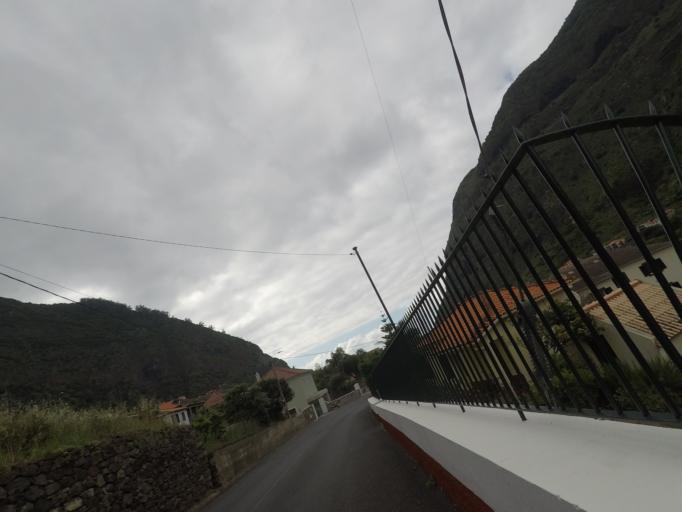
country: PT
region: Madeira
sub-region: Sao Vicente
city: Sao Vicente
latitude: 32.7996
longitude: -17.0441
